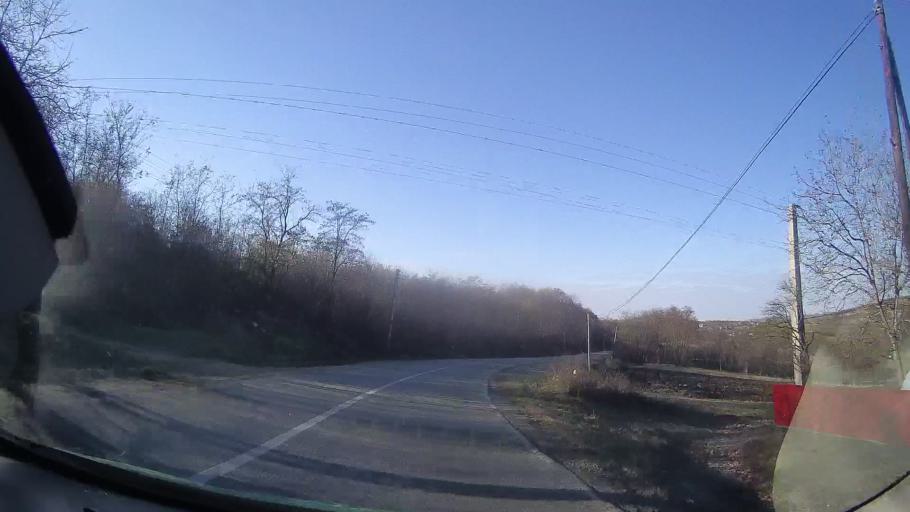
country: RO
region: Cluj
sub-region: Comuna Mociu
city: Mociu
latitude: 46.7917
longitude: 24.0651
